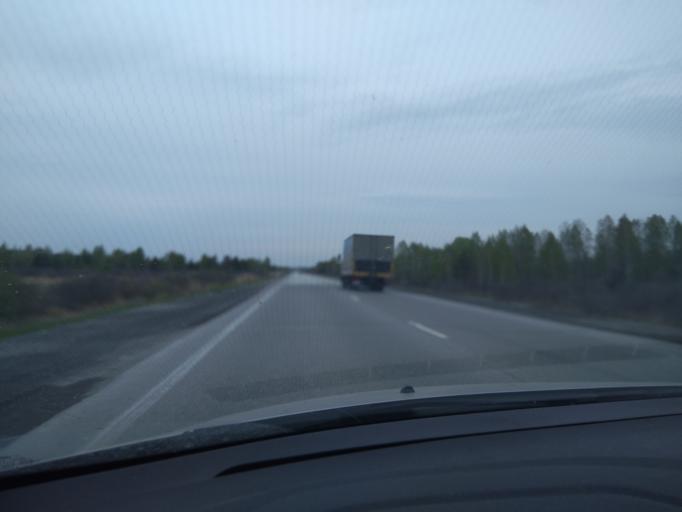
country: RU
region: Sverdlovsk
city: Yelanskiy
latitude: 56.8209
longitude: 62.5481
